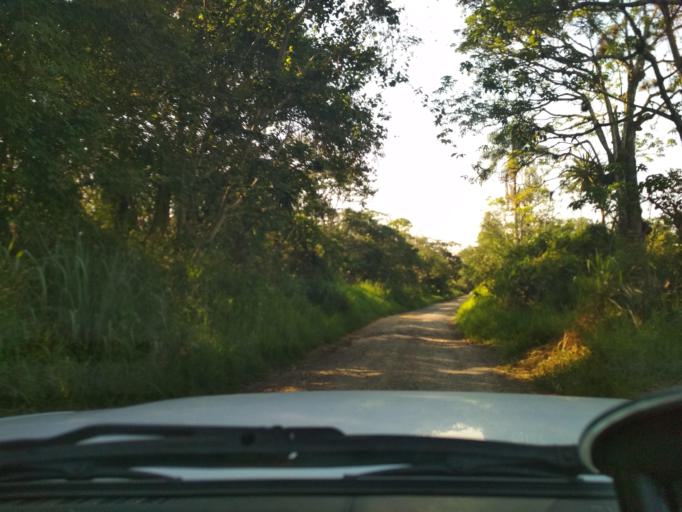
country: MX
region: Veracruz
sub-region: Fortin
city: Fraccionamiento Villas de la Llave
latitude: 18.9198
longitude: -96.9890
